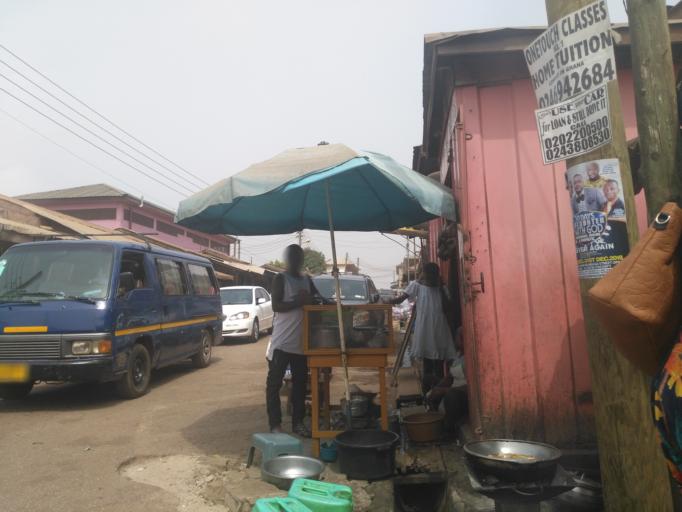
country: GH
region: Ashanti
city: Kumasi
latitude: 6.7014
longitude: -1.6183
